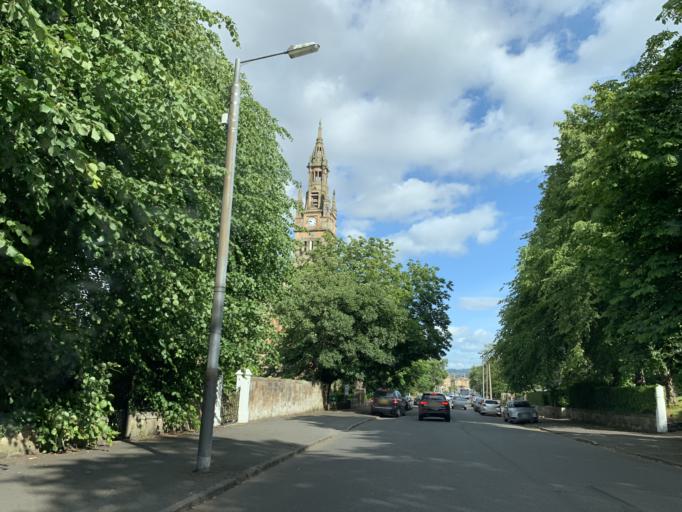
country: GB
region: Scotland
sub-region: Glasgow City
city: Glasgow
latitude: 55.8408
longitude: -4.2790
